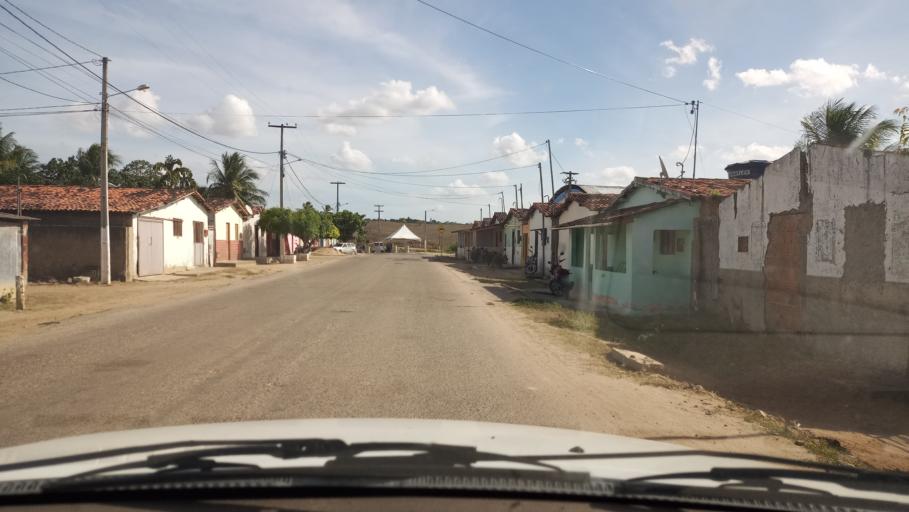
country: BR
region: Rio Grande do Norte
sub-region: Goianinha
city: Goianinha
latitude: -6.3296
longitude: -35.3041
